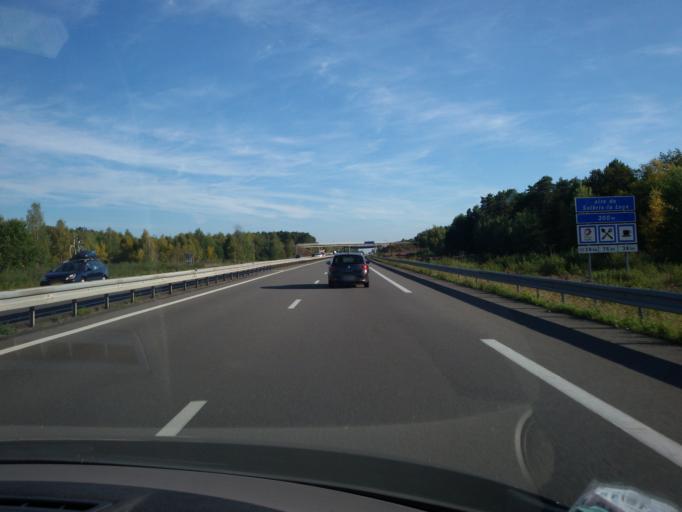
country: FR
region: Centre
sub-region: Departement du Loir-et-Cher
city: Theillay
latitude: 47.3419
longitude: 2.0480
